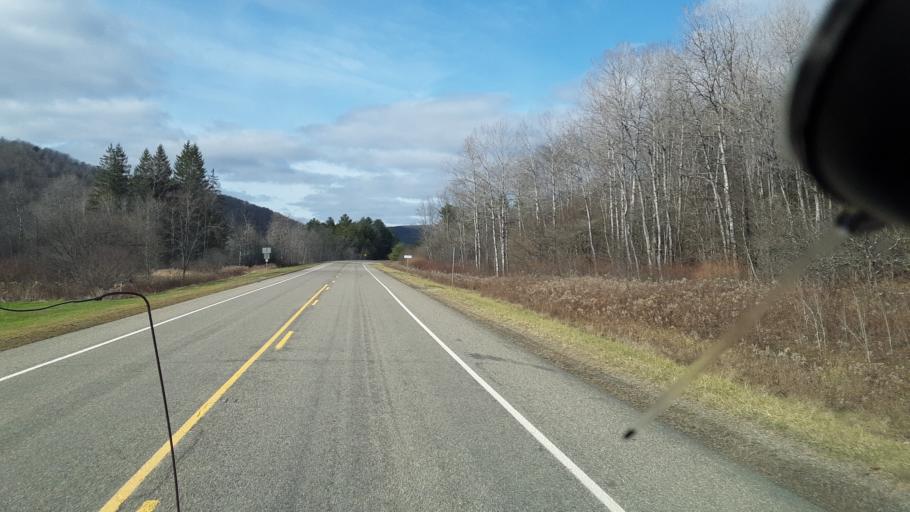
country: US
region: Pennsylvania
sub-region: Potter County
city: Galeton
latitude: 41.7784
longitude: -77.7264
